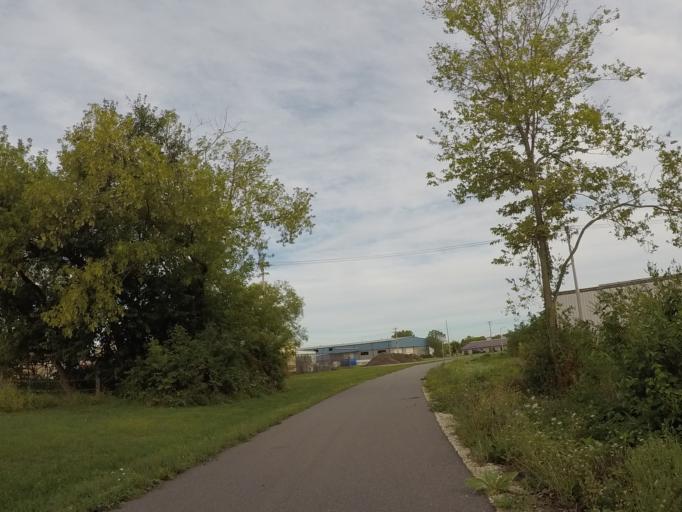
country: US
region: Wisconsin
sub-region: Sauk County
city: Sauk City
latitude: 43.2663
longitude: -89.7287
